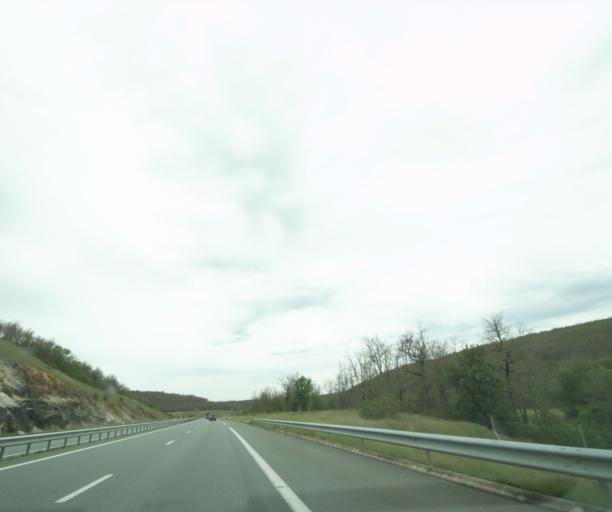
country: FR
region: Midi-Pyrenees
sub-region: Departement du Lot
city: Le Vigan
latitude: 44.7760
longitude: 1.5356
